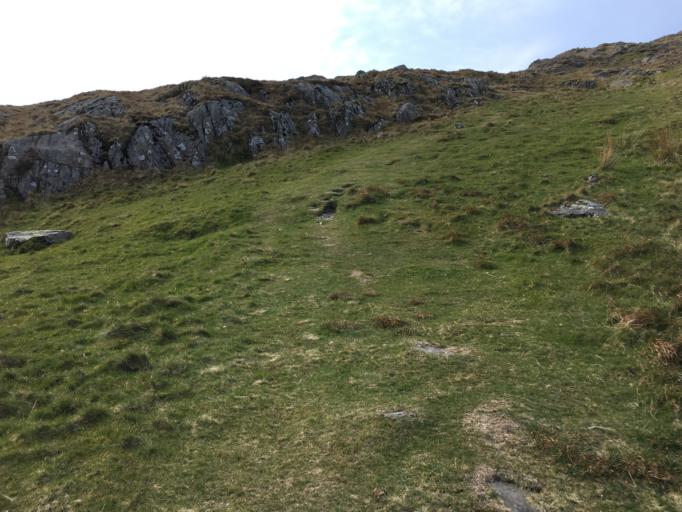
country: GB
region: Wales
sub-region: Gwynedd
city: Porthmadog
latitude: 53.0093
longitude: -4.1271
